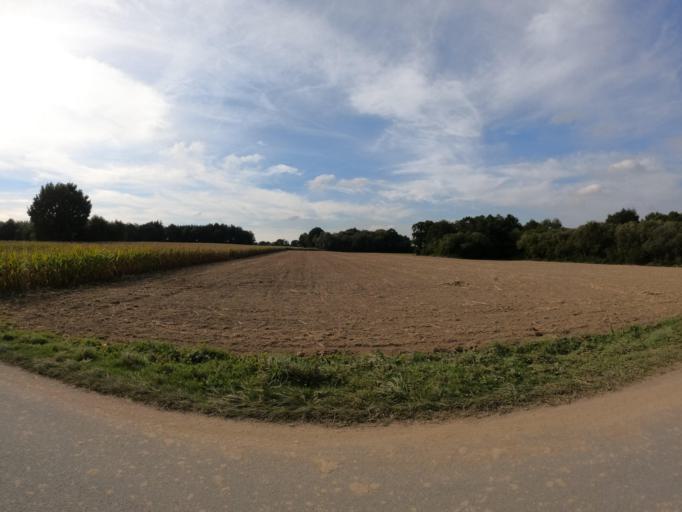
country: FR
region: Brittany
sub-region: Departement du Morbihan
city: Caro
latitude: 47.8842
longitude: -2.3498
